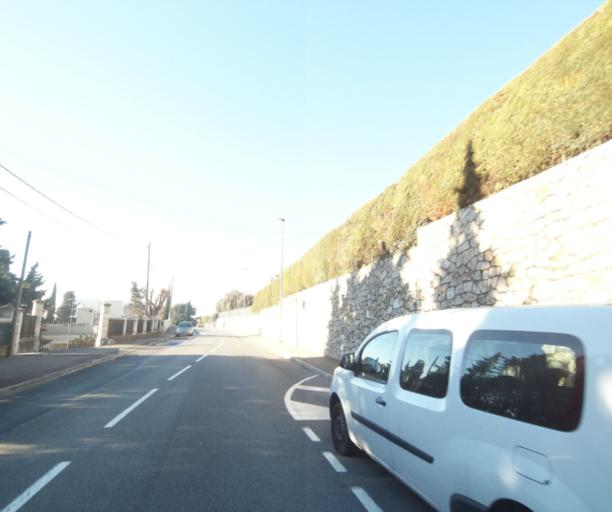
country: FR
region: Provence-Alpes-Cote d'Azur
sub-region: Departement des Alpes-Maritimes
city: Antibes
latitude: 43.5835
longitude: 7.1000
